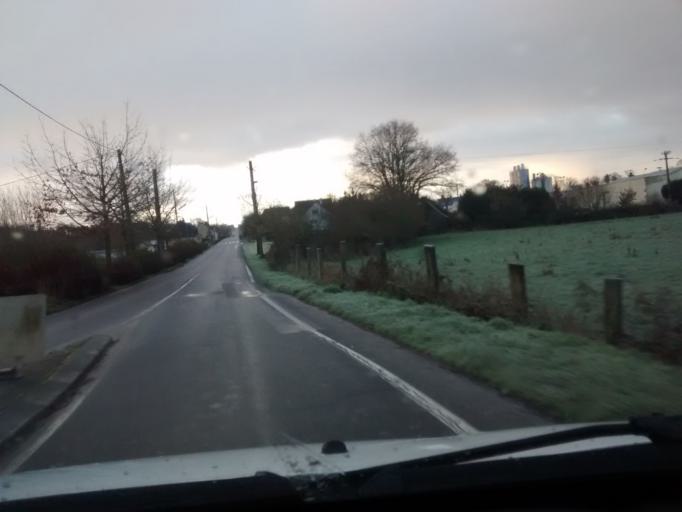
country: FR
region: Brittany
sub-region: Departement d'Ille-et-Vilaine
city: Bais
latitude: 48.0063
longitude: -1.2892
